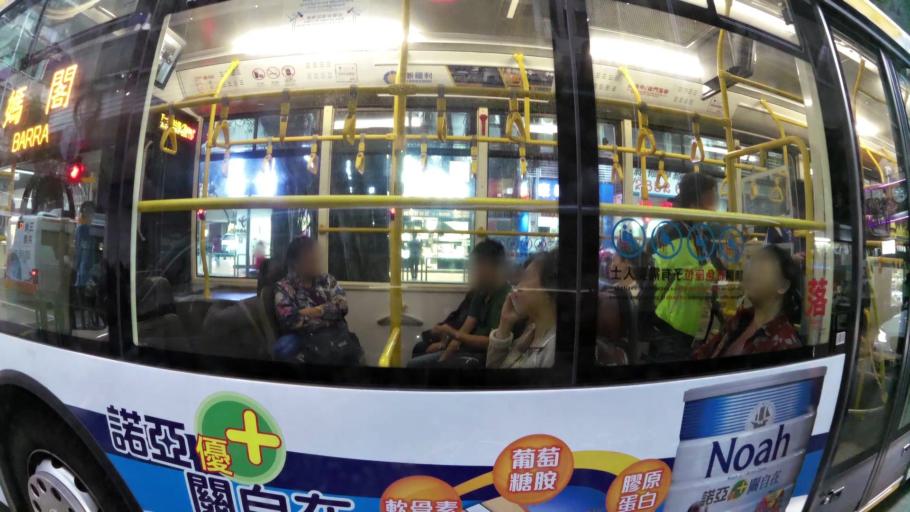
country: MO
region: Macau
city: Macau
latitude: 22.2034
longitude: 113.5466
